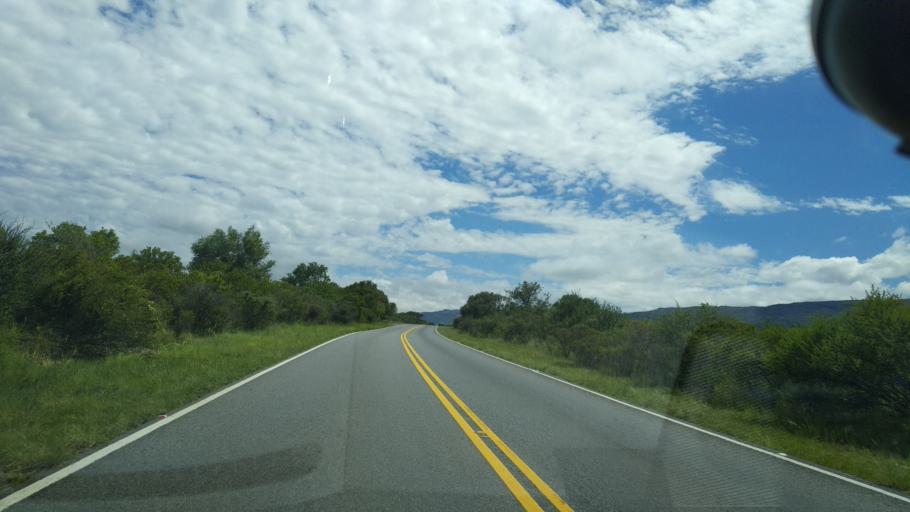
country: AR
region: Cordoba
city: Mina Clavero
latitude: -31.7534
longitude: -64.9520
